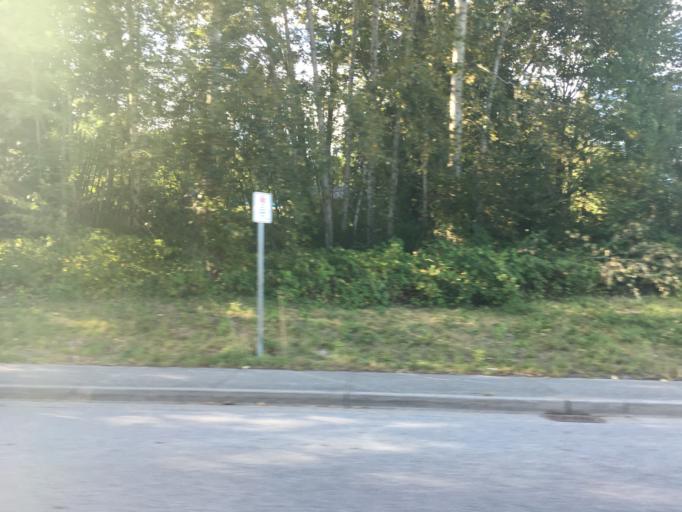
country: CA
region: British Columbia
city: Port Moody
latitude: 49.2436
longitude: -122.8171
